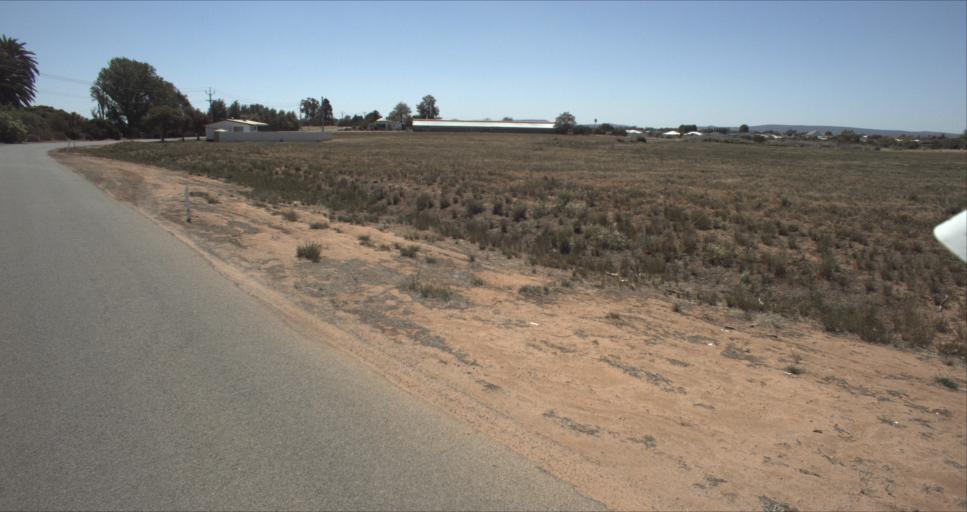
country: AU
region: New South Wales
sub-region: Leeton
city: Leeton
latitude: -34.5435
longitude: 146.3944
